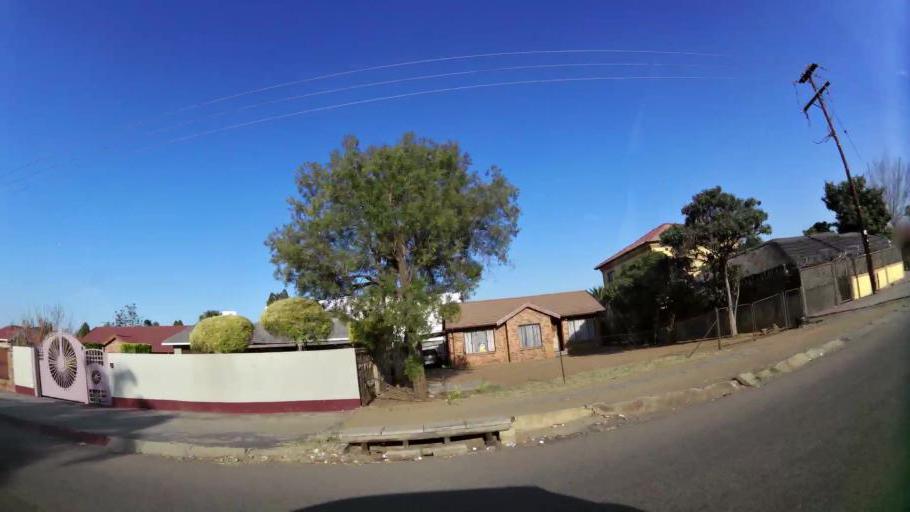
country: ZA
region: North-West
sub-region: Bojanala Platinum District Municipality
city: Rustenburg
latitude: -25.6500
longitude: 27.2181
